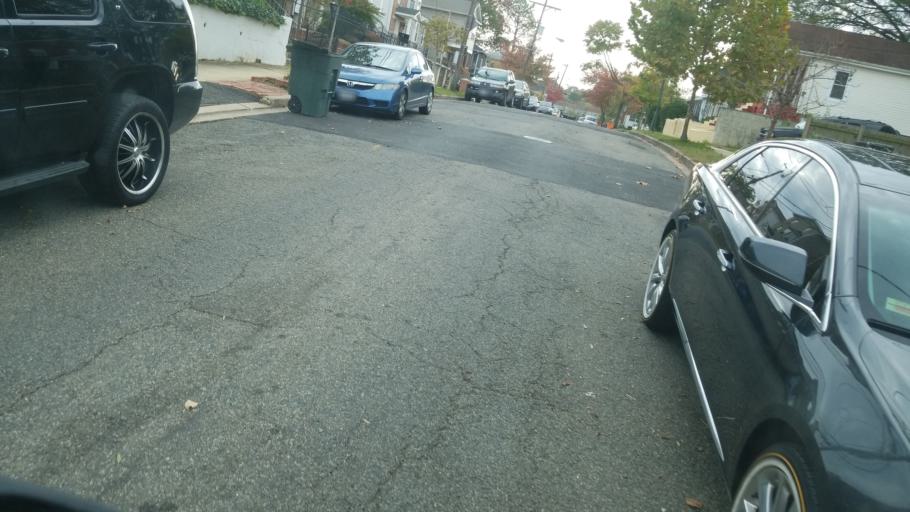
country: US
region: Maryland
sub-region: Prince George's County
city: Capitol Heights
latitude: 38.8924
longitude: -76.9205
